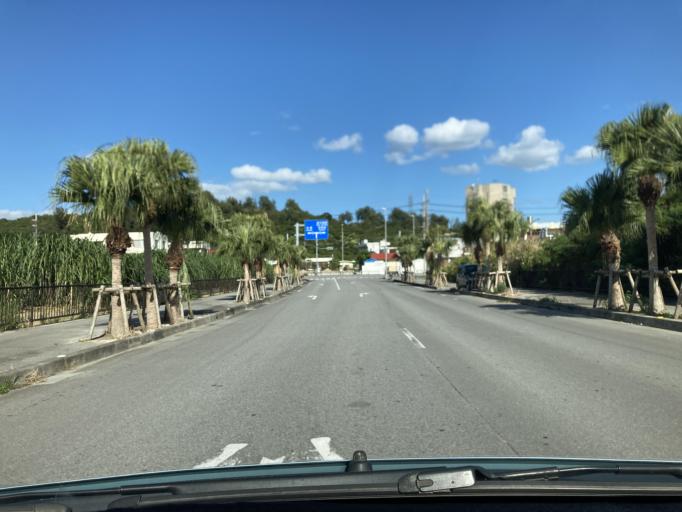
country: JP
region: Okinawa
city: Katsuren-haebaru
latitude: 26.3401
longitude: 127.8704
